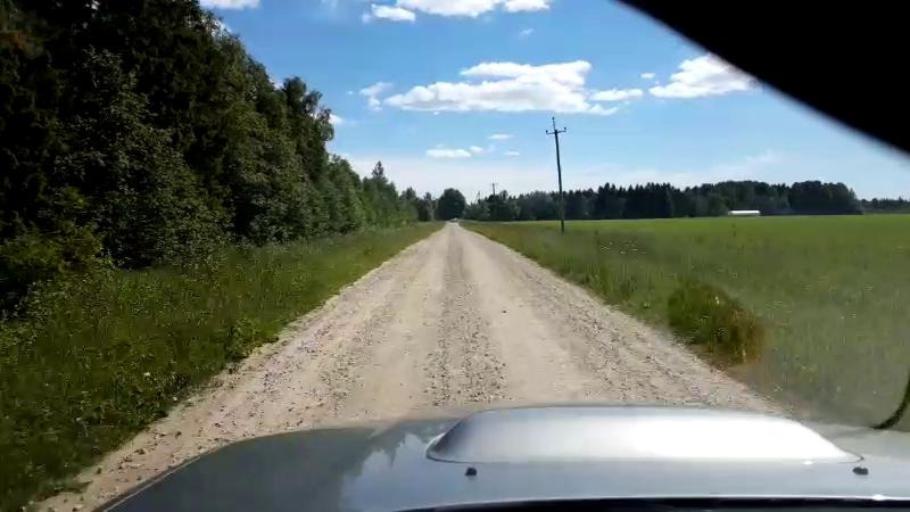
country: EE
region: Paernumaa
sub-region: Halinga vald
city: Parnu-Jaagupi
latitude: 58.5365
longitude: 24.5433
